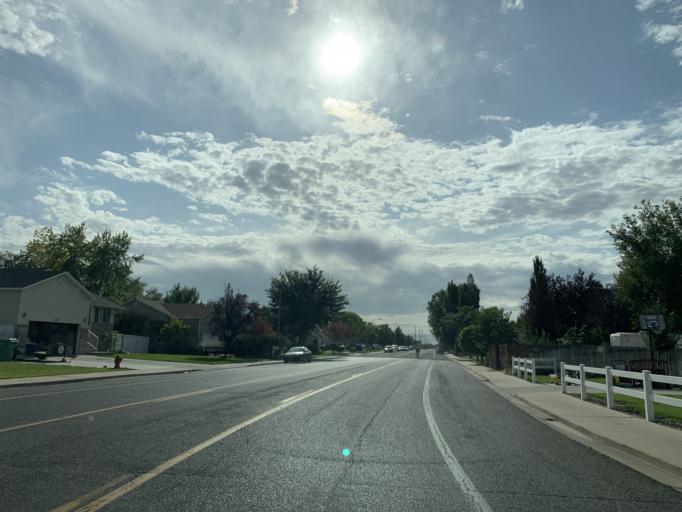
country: US
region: Utah
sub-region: Utah County
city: Provo
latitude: 40.2185
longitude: -111.6729
